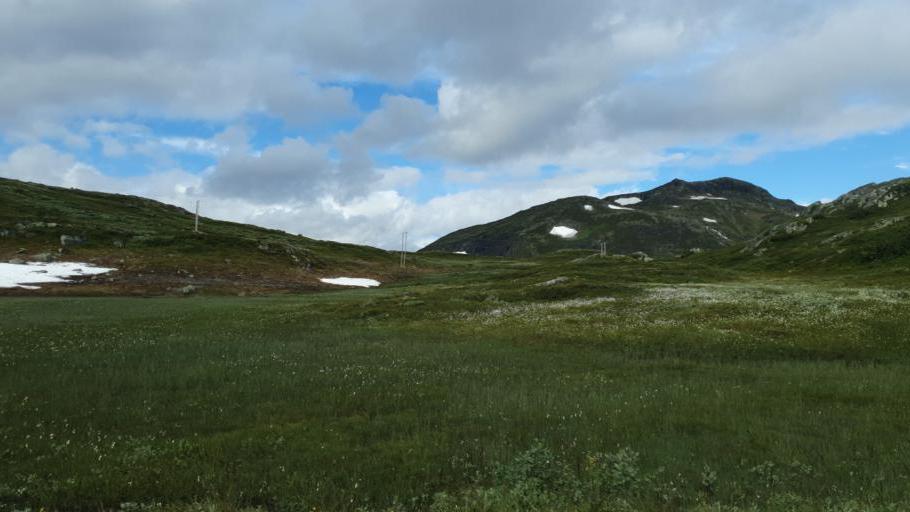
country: NO
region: Oppland
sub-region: Vestre Slidre
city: Slidre
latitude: 61.3236
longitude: 8.8038
